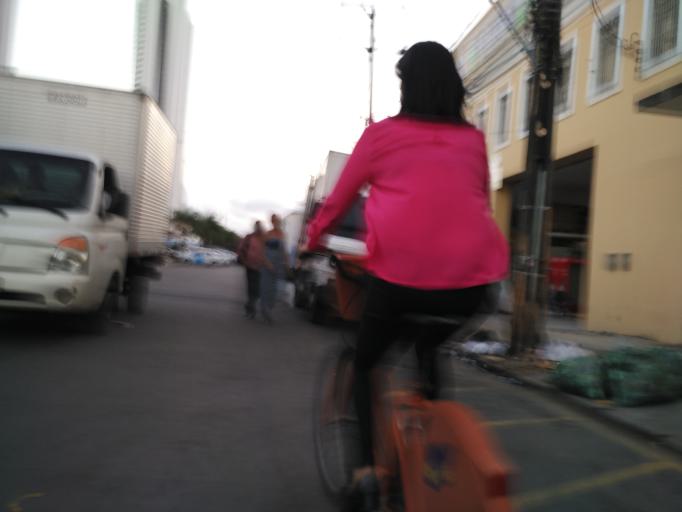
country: BR
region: Pernambuco
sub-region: Recife
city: Recife
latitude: -8.0689
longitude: -34.8765
